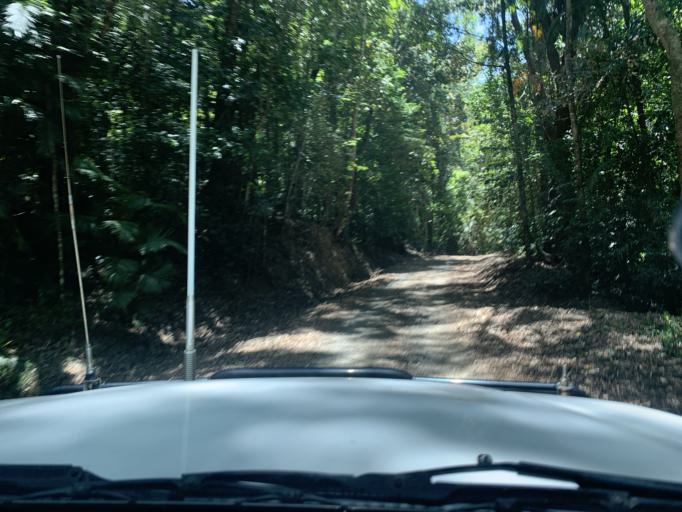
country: AU
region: Queensland
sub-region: Cairns
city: Redlynch
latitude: -16.9641
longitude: 145.6459
